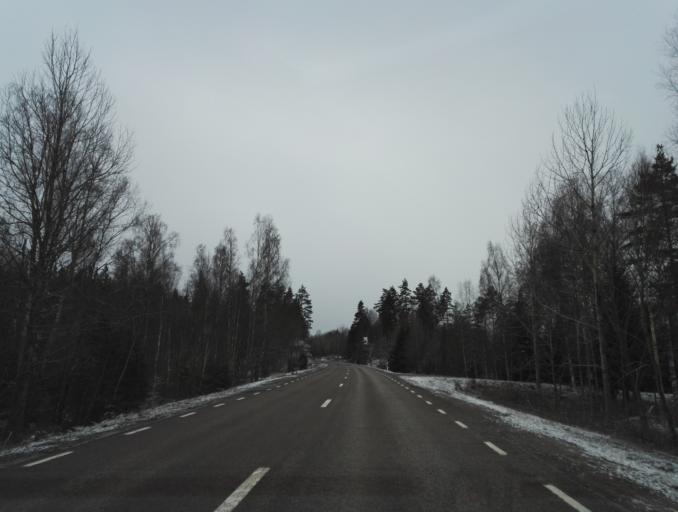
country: SE
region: Kalmar
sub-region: Hultsfreds Kommun
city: Virserum
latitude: 57.2533
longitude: 15.5431
